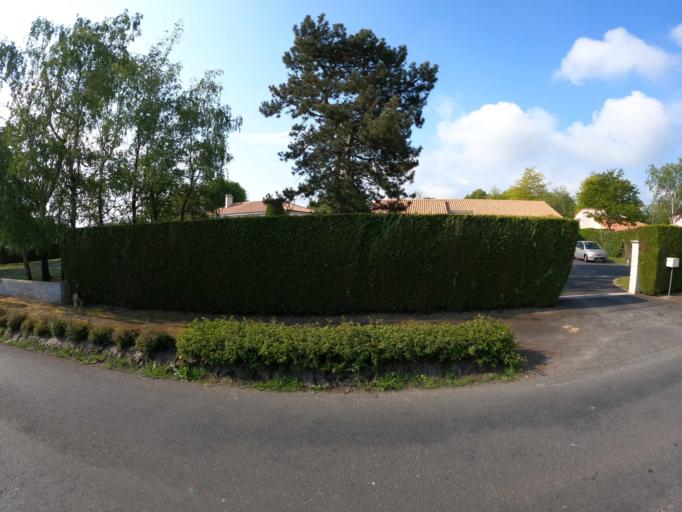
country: FR
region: Pays de la Loire
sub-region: Departement de Maine-et-Loire
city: La Romagne
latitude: 47.0638
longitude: -1.0293
